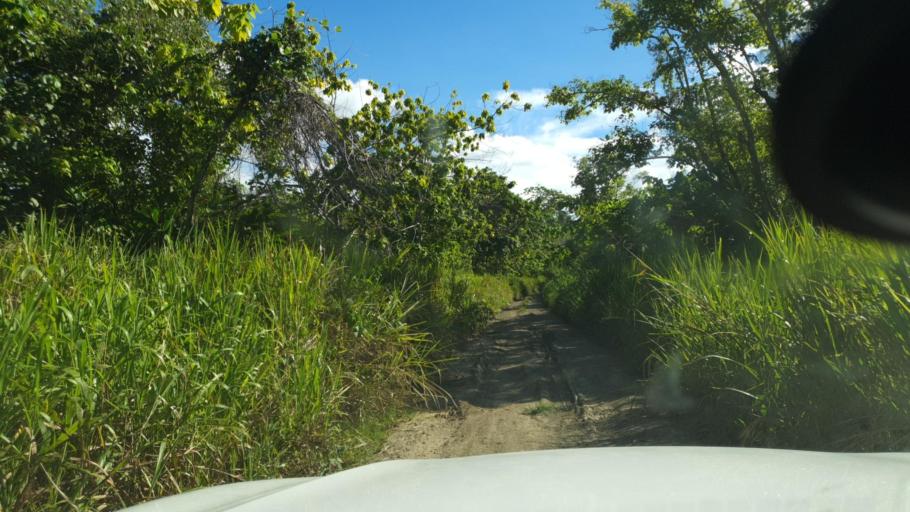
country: SB
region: Guadalcanal
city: Honiara
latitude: -9.4243
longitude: 160.1751
